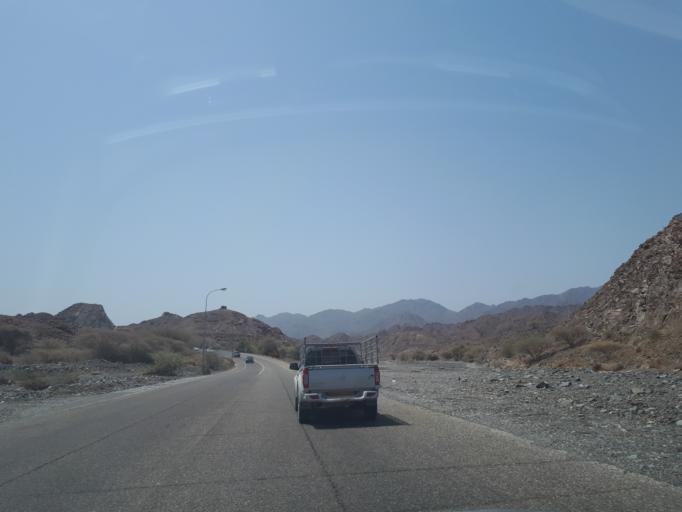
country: OM
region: Muhafazat ad Dakhiliyah
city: Sufalat Sama'il
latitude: 23.2022
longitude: 58.0821
